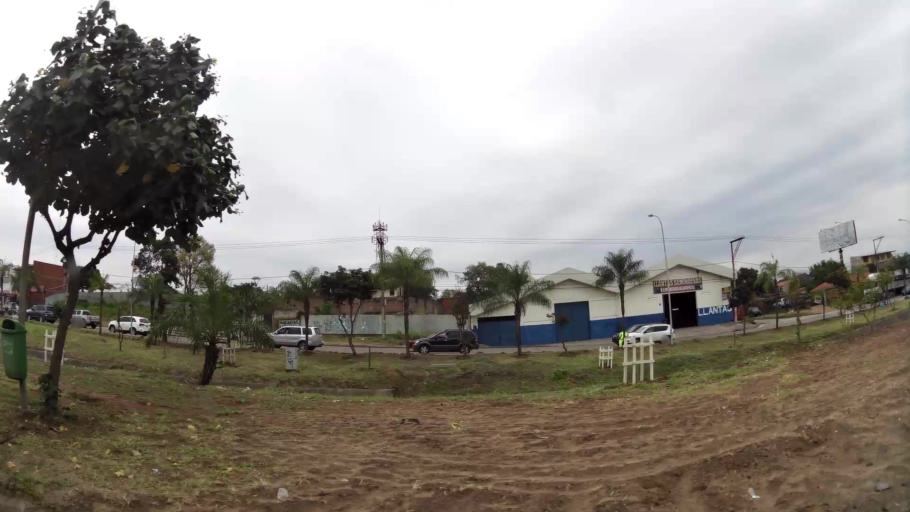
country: BO
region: Santa Cruz
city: Santa Cruz de la Sierra
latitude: -17.7498
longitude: -63.1830
